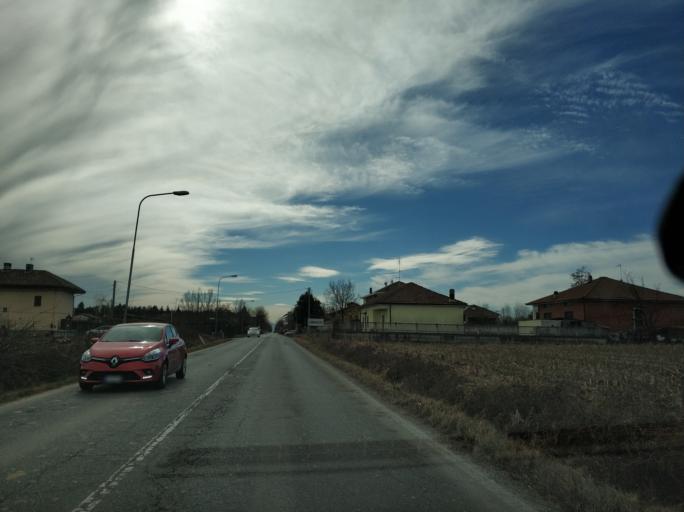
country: IT
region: Piedmont
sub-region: Provincia di Torino
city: Lombardore
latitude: 45.2273
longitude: 7.7317
